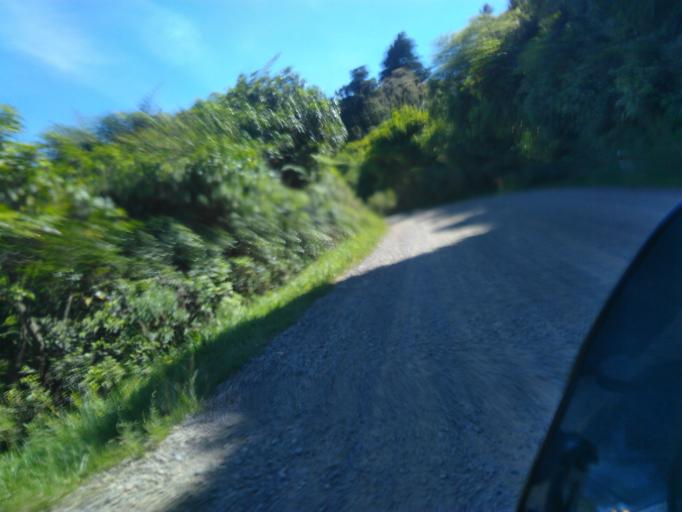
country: NZ
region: Hawke's Bay
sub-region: Wairoa District
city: Wairoa
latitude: -38.7948
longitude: 177.1249
